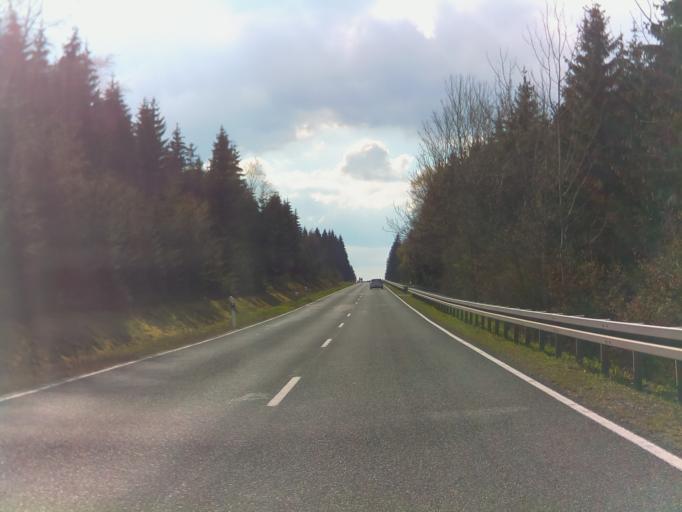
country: DE
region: Bavaria
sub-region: Upper Franconia
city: Tettau
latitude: 50.4897
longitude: 11.2878
